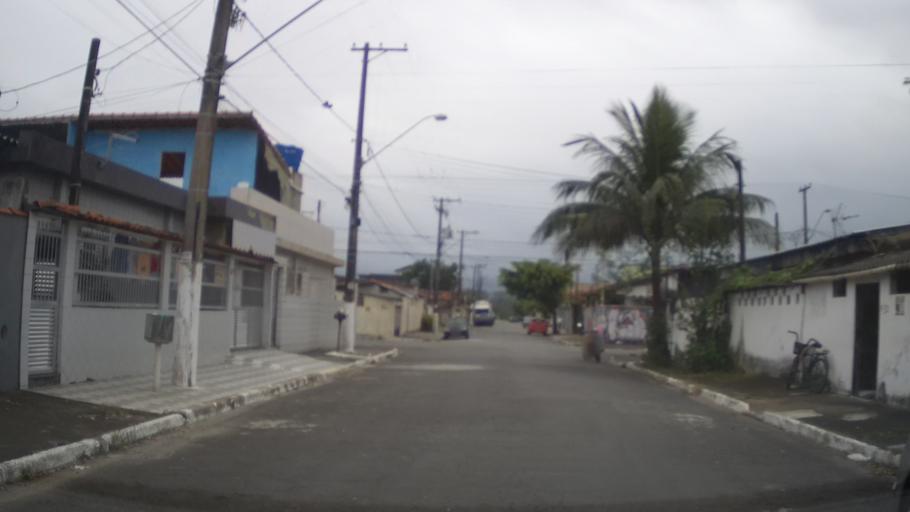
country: BR
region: Sao Paulo
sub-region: Praia Grande
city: Praia Grande
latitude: -24.0021
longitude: -46.4314
